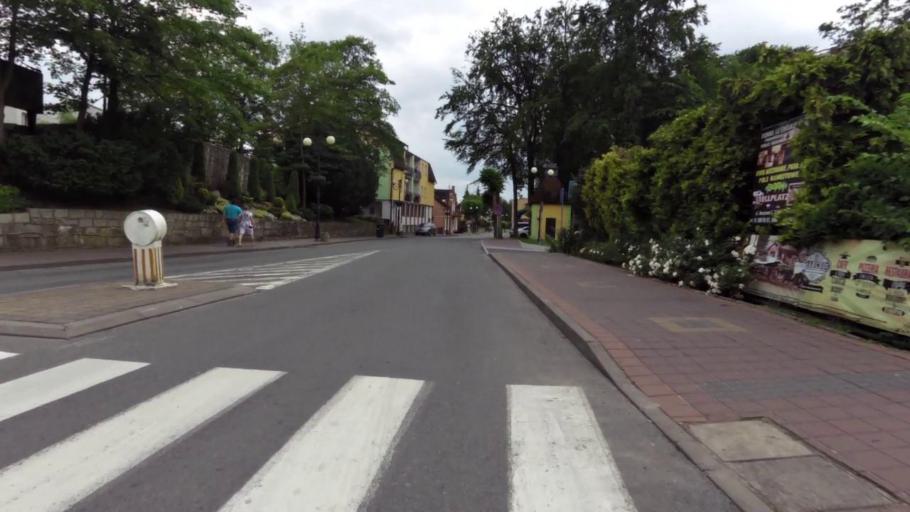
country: PL
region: West Pomeranian Voivodeship
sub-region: Powiat gryficki
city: Rewal
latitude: 54.0811
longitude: 15.0145
